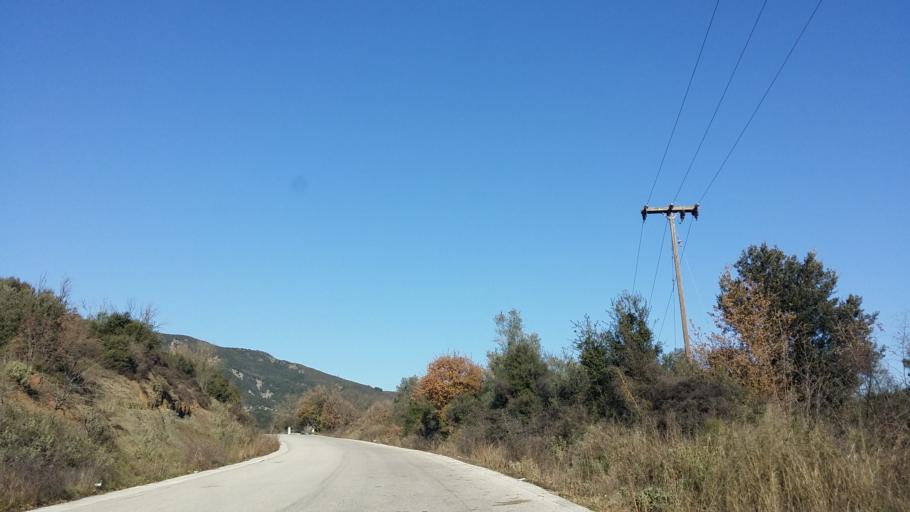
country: GR
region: West Greece
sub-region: Nomos Aitolias kai Akarnanias
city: Sardinia
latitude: 38.8737
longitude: 21.3406
